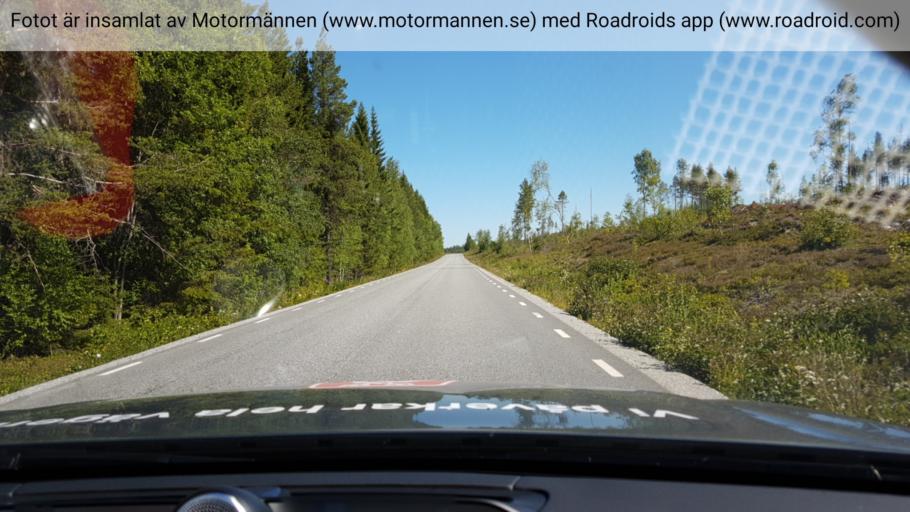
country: SE
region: Jaemtland
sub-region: Braecke Kommun
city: Braecke
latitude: 63.0893
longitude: 15.4327
